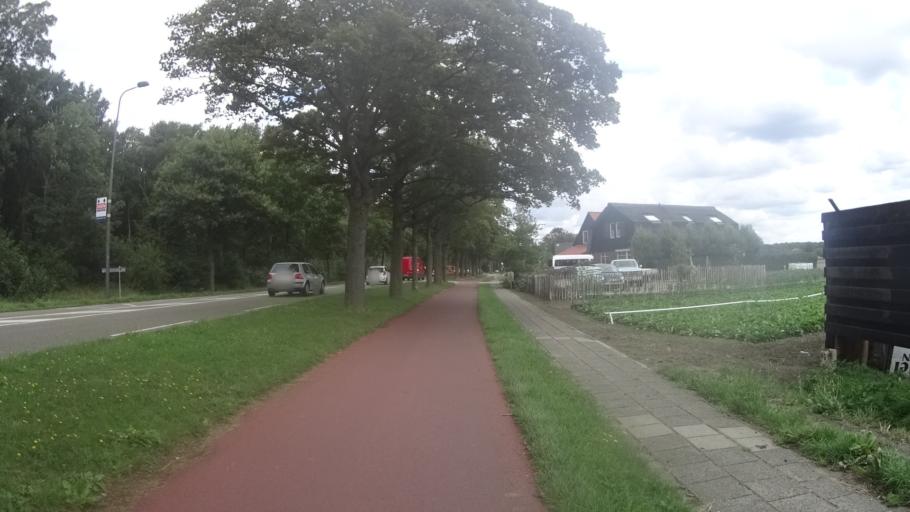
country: NL
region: North Holland
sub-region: Gemeente Castricum
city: Castricum
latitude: 52.5295
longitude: 4.6523
